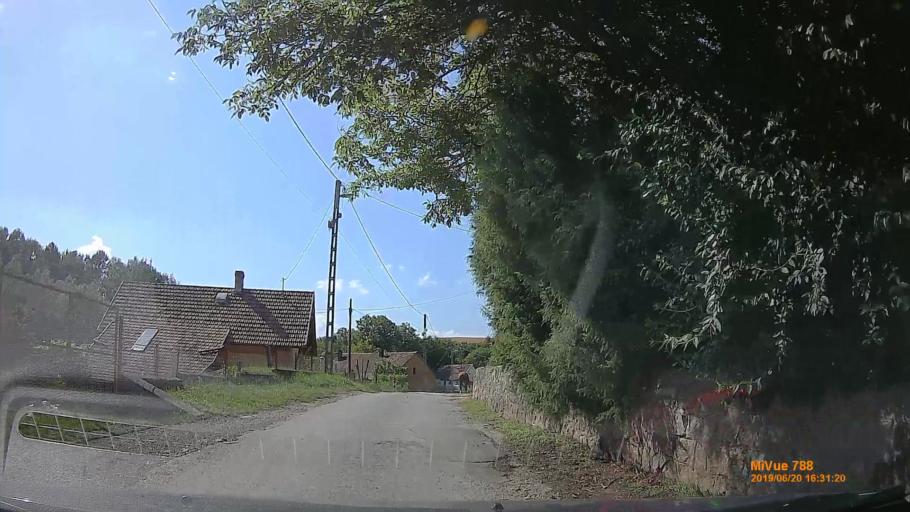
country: HU
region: Baranya
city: Buekkoesd
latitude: 46.1720
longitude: 18.0512
